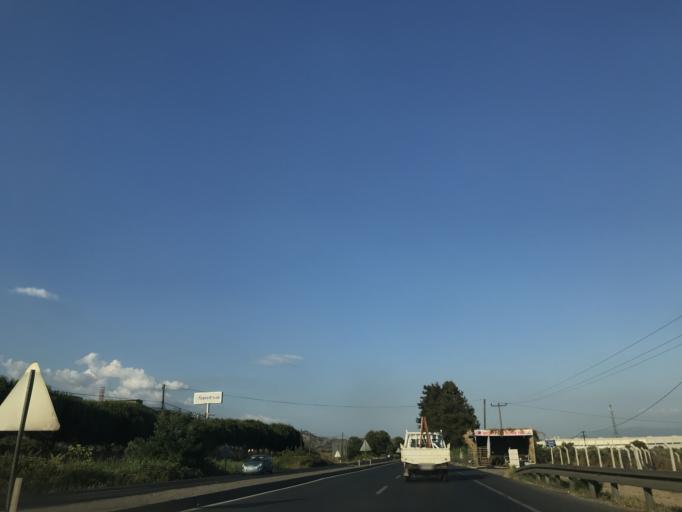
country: TR
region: Aydin
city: Umurlu
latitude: 37.8557
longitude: 27.9853
